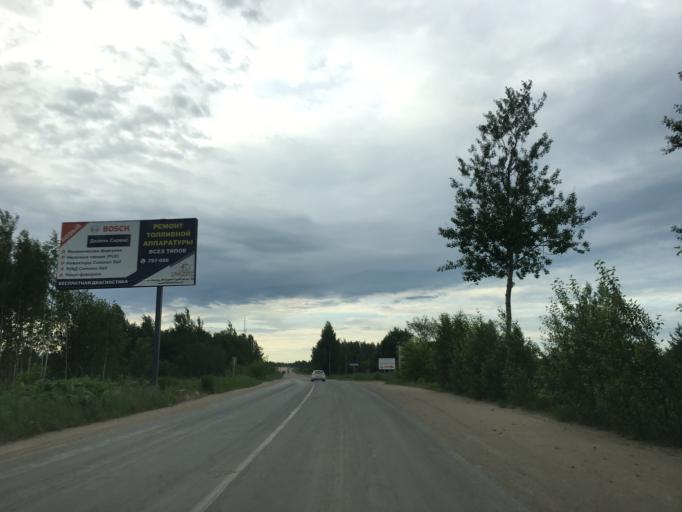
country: RU
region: Pskov
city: Pskov
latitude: 57.8524
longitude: 28.3078
